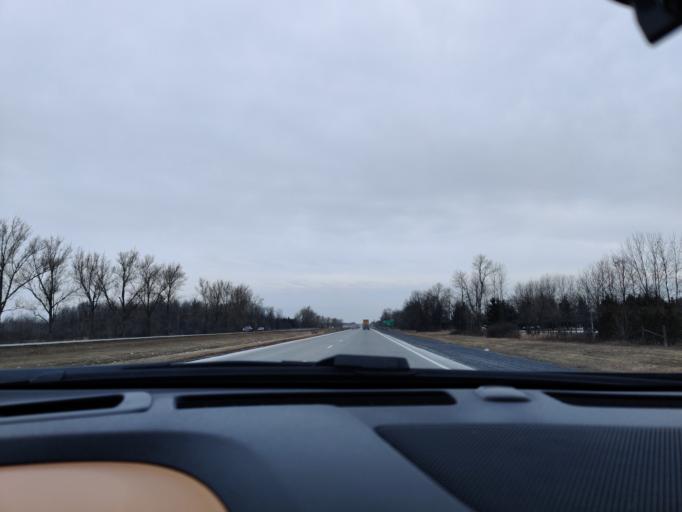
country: US
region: New York
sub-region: St. Lawrence County
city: Massena
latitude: 45.0188
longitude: -74.9790
